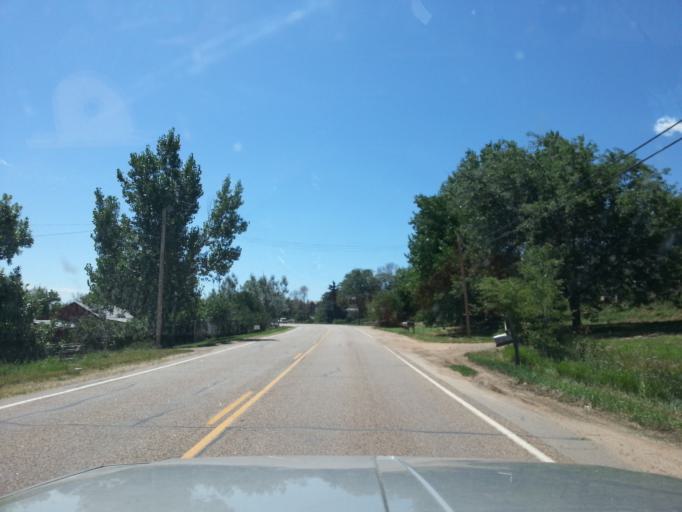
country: US
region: Colorado
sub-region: Larimer County
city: Loveland
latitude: 40.4360
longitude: -105.1972
